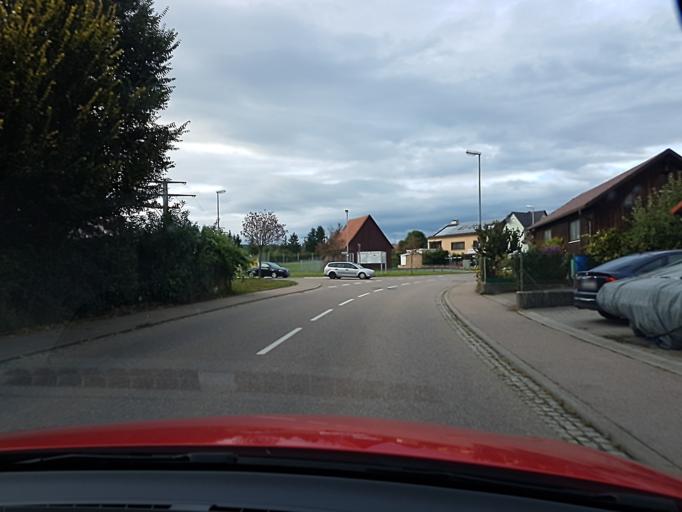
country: DE
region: Baden-Wuerttemberg
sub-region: Karlsruhe Region
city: Sternenfels
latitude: 49.0065
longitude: 8.8589
